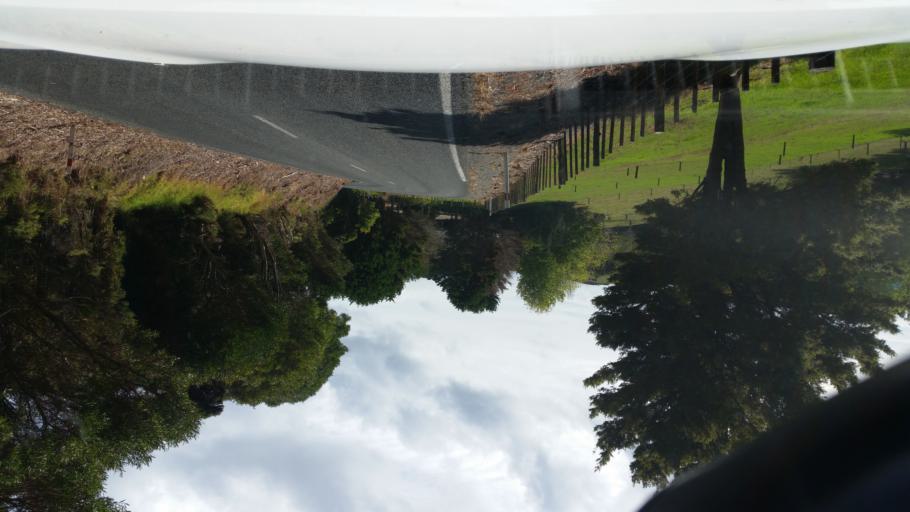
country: NZ
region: Auckland
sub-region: Auckland
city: Wellsford
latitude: -36.0861
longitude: 174.5500
